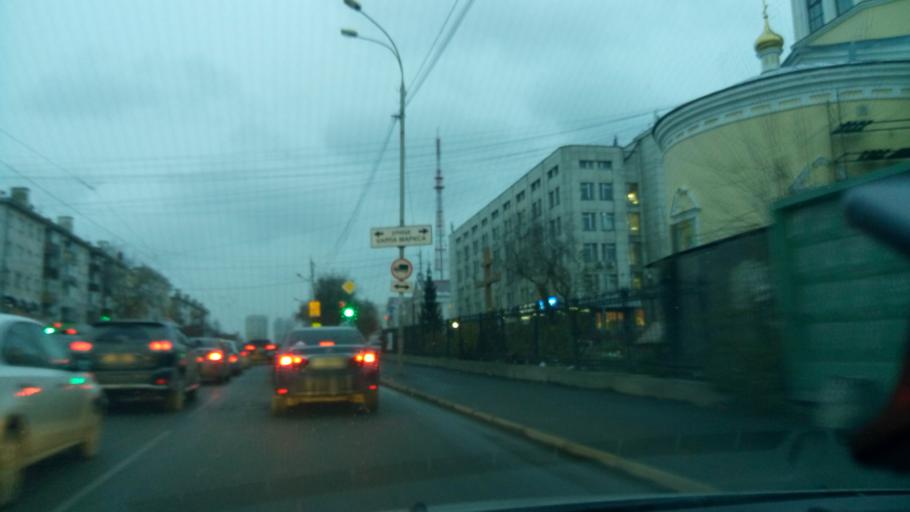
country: RU
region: Sverdlovsk
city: Yekaterinburg
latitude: 56.8323
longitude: 60.6232
